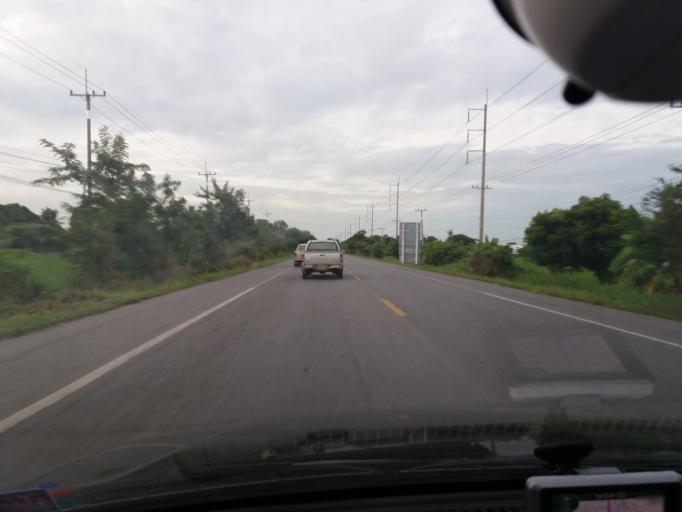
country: TH
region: Suphan Buri
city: U Thong
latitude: 14.5059
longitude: 99.9173
